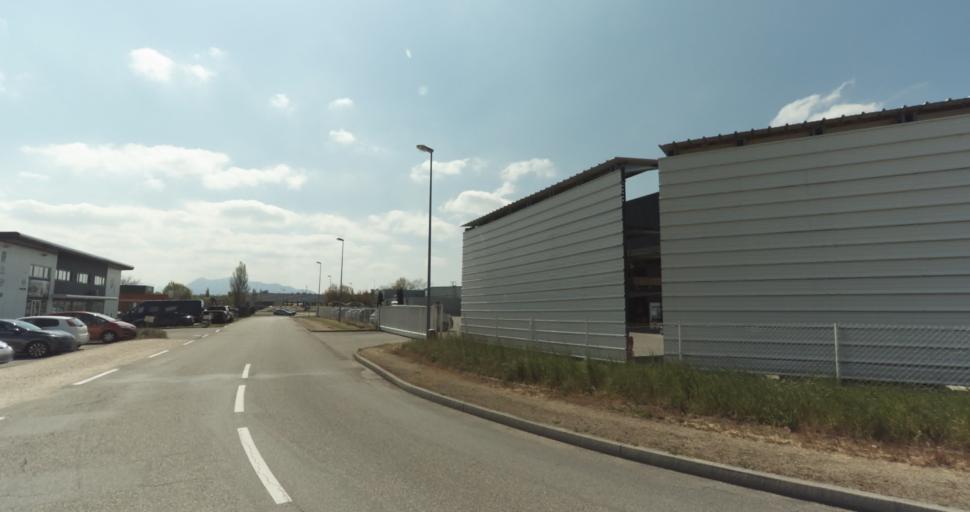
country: FR
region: Rhone-Alpes
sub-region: Departement de l'Isere
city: Saint-Marcellin
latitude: 45.1409
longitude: 5.3286
